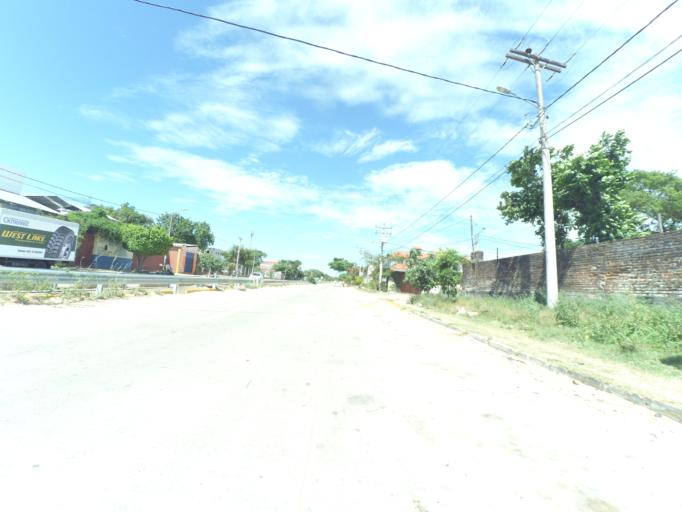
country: BO
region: Santa Cruz
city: Santa Cruz de la Sierra
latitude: -17.8012
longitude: -63.2160
